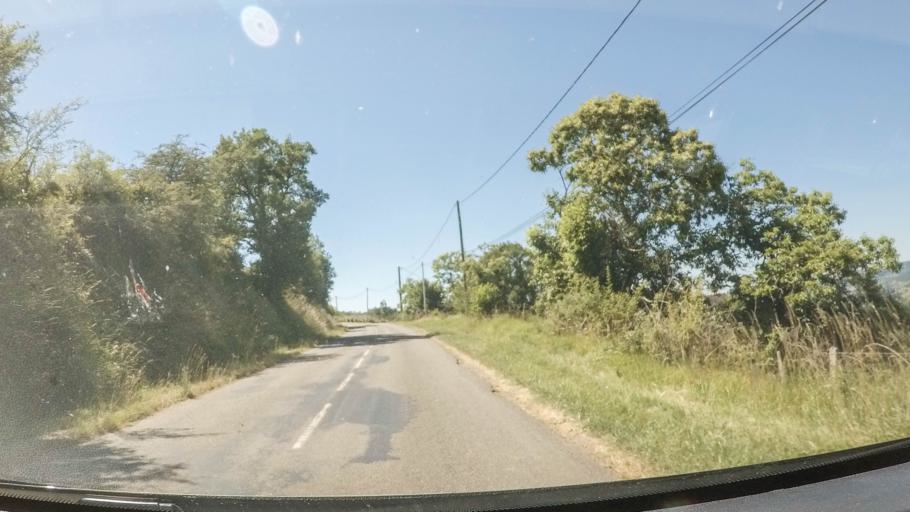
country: FR
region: Midi-Pyrenees
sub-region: Departement de l'Aveyron
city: Saint-Christophe-Vallon
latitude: 44.4719
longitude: 2.3622
